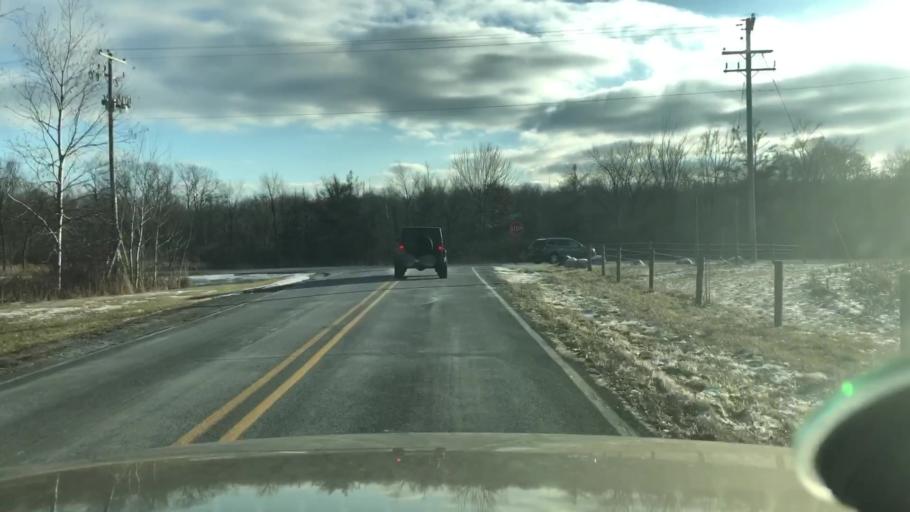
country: US
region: Michigan
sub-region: Jackson County
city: Vandercook Lake
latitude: 42.0979
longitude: -84.4511
